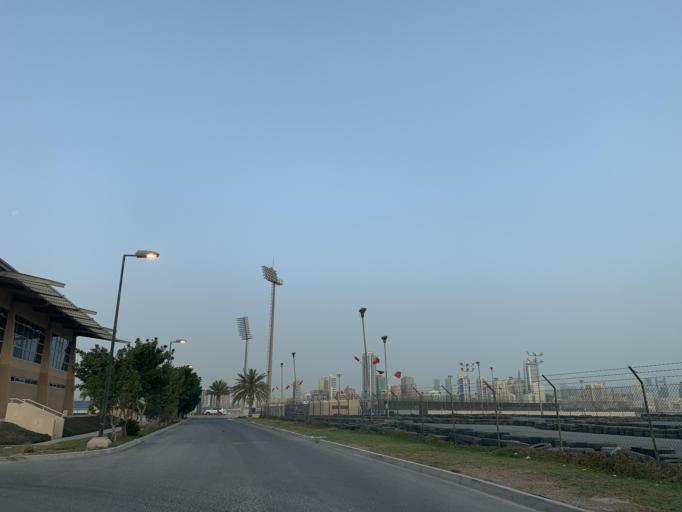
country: BH
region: Manama
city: Manama
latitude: 26.2259
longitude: 50.6103
